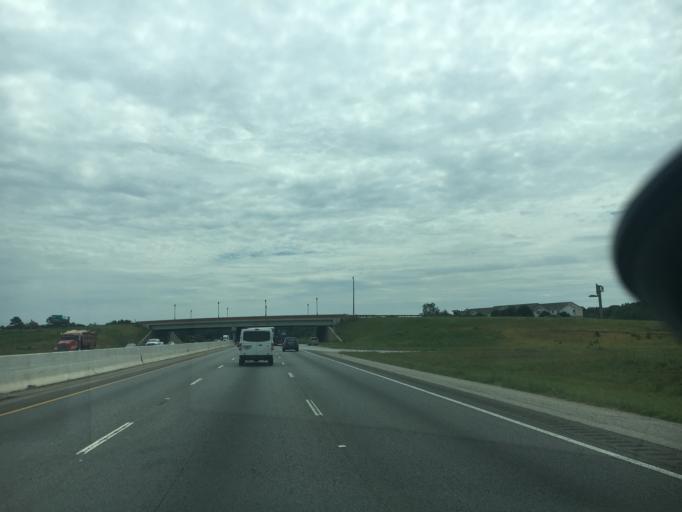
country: US
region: South Carolina
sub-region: Greenville County
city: Simpsonville
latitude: 34.7390
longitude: -82.2733
